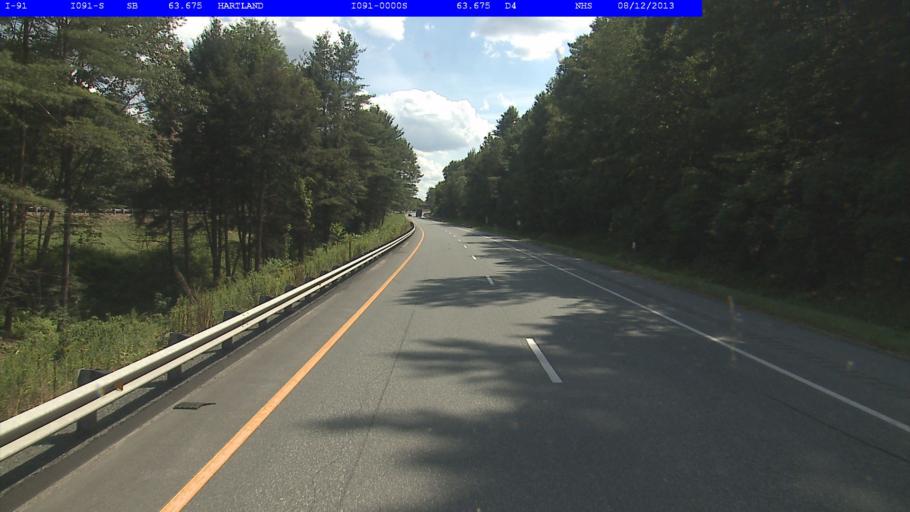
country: US
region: Vermont
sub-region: Windsor County
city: Windsor
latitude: 43.5705
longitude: -72.3865
